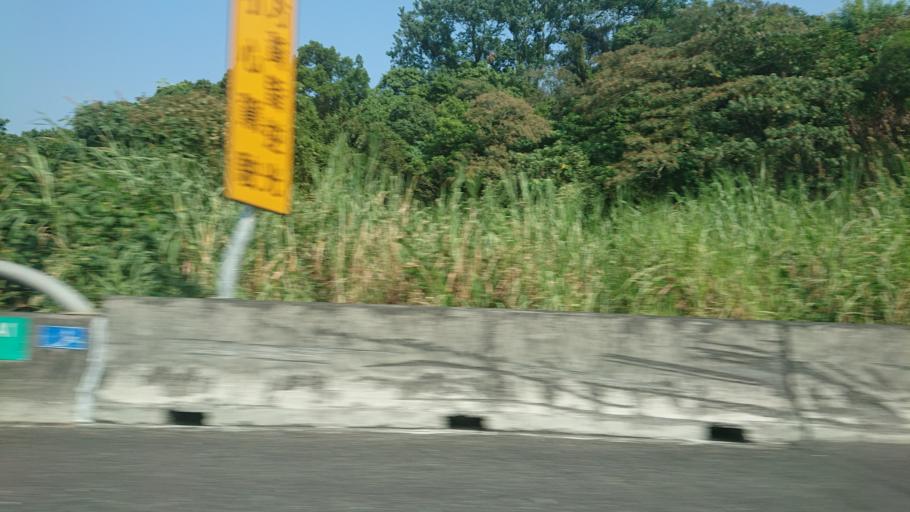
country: TW
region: Taiwan
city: Lugu
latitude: 23.7786
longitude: 120.6804
